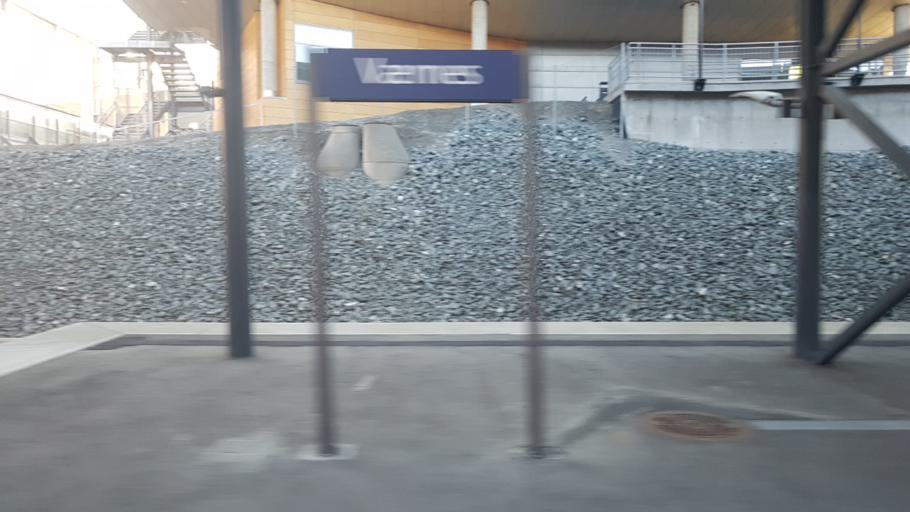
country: NO
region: Nord-Trondelag
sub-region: Stjordal
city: Stjordal
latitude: 63.4481
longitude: 10.8954
